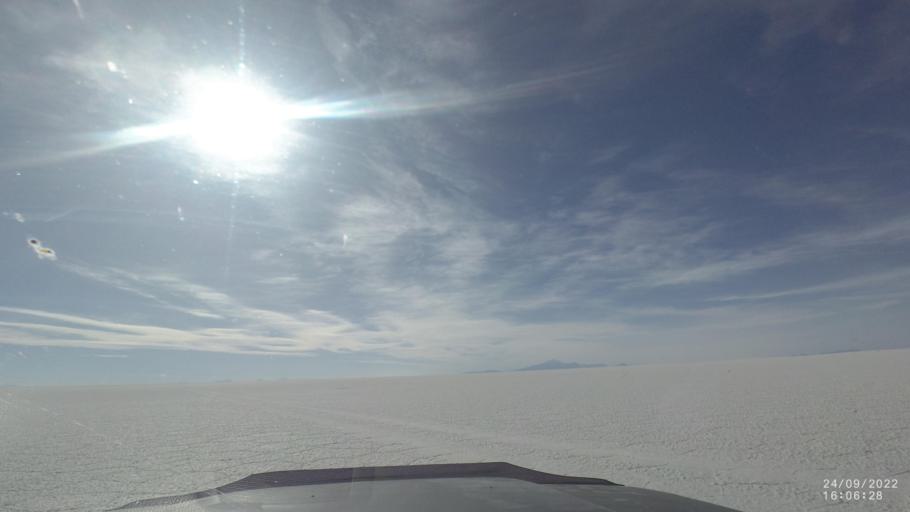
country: BO
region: Potosi
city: Colchani
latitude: -20.3057
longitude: -67.2942
